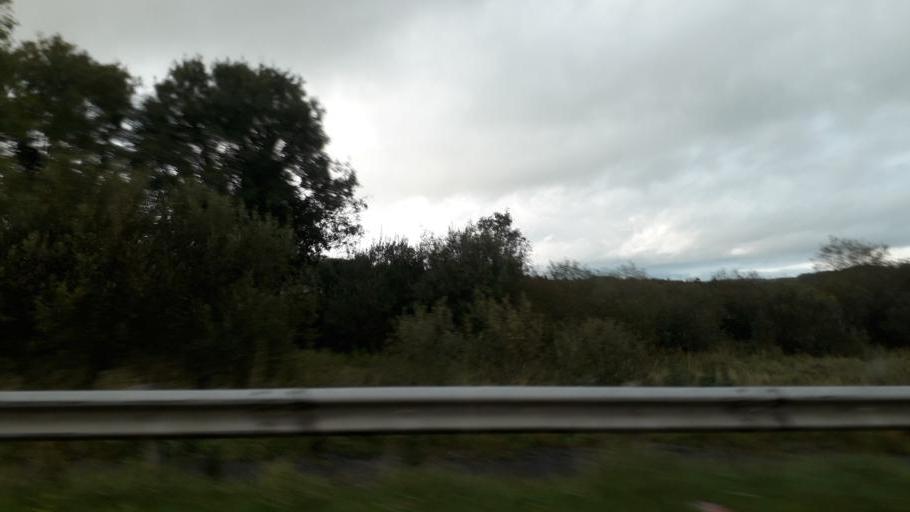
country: IE
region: Leinster
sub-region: An Longfort
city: Lanesborough
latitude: 53.7649
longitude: -8.0718
